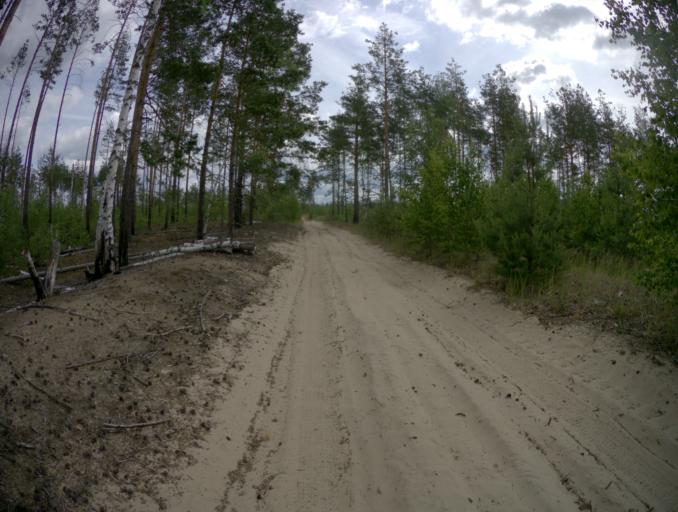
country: RU
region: Nizjnij Novgorod
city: Frolishchi
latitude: 56.5121
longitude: 42.5052
